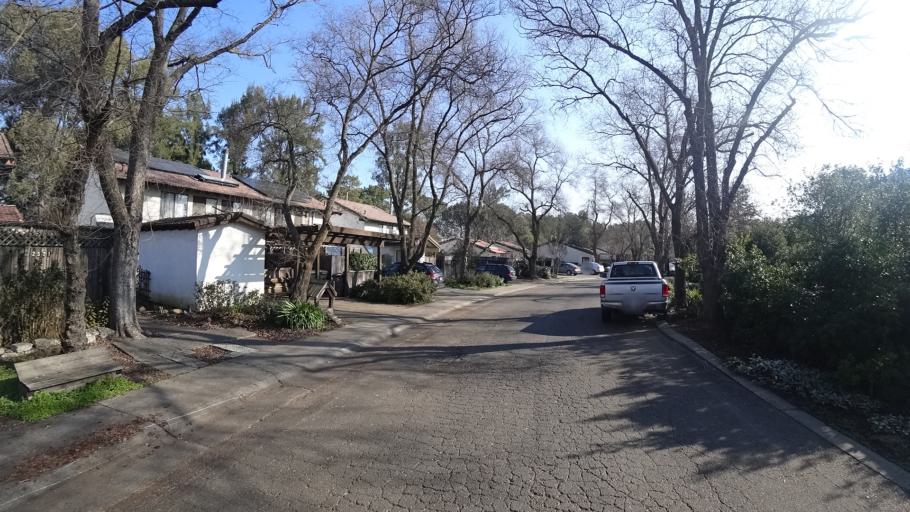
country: US
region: California
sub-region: Yolo County
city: Davis
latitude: 38.5531
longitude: -121.7823
